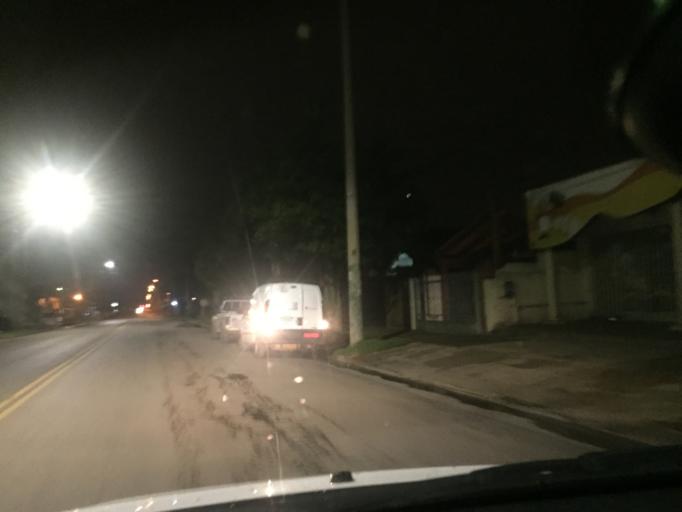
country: AR
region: Cordoba
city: Villa Allende
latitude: -31.3078
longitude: -64.2882
